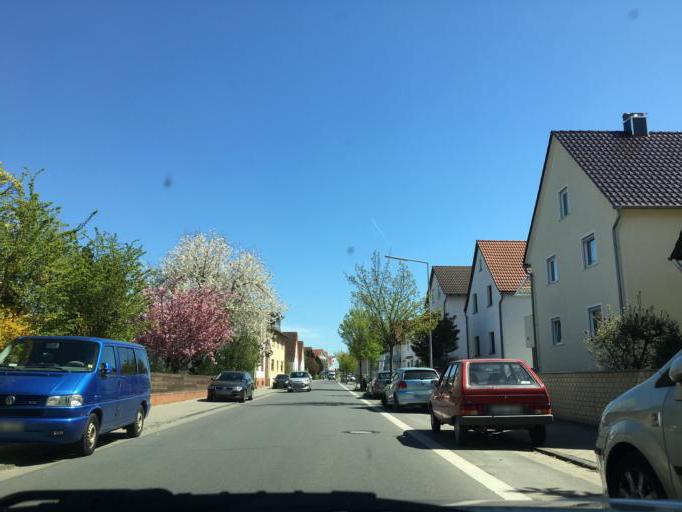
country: DE
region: Hesse
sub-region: Regierungsbezirk Darmstadt
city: Gross-Zimmern
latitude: 49.8725
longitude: 8.8247
